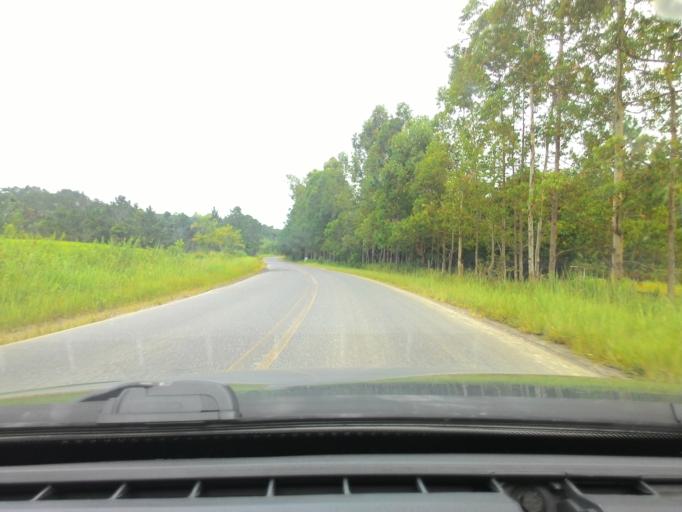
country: BR
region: Sao Paulo
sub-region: Pariquera-Acu
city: Pariquera Acu
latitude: -24.7318
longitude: -47.8344
